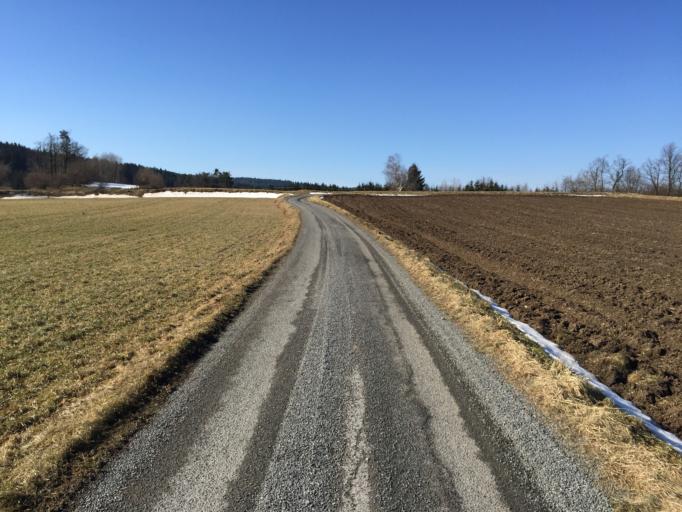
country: AT
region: Lower Austria
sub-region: Politischer Bezirk Gmund
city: Weitra
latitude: 48.6681
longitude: 14.9324
